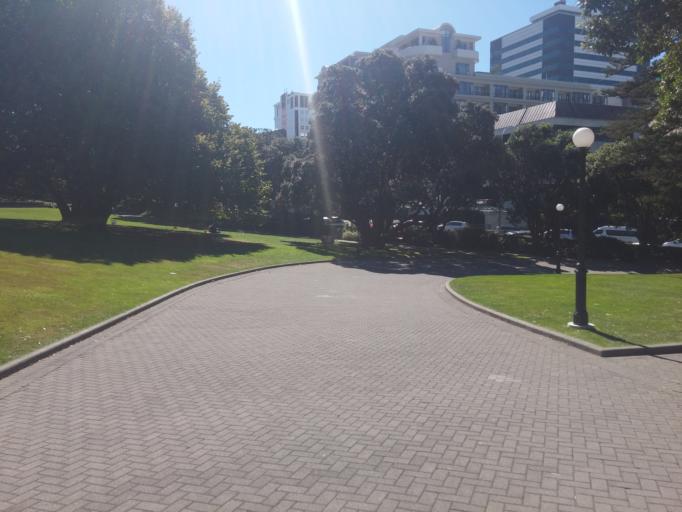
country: NZ
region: Wellington
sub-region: Wellington City
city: Wellington
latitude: -41.2785
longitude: 174.7774
